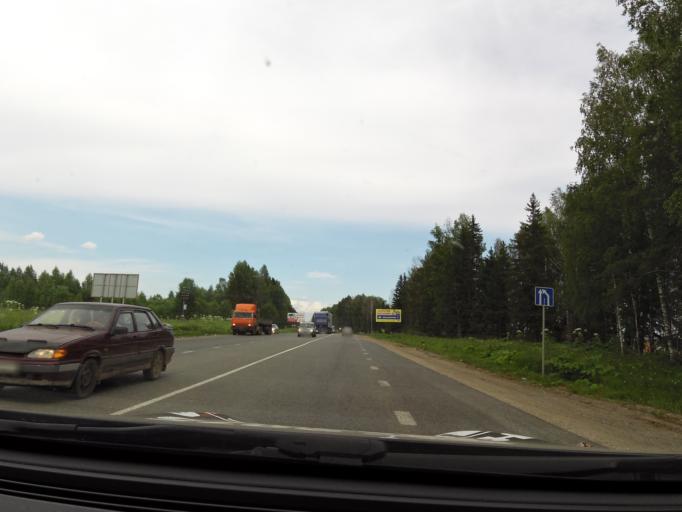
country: RU
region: Kirov
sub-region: Kirovo-Chepetskiy Rayon
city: Kirov
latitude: 58.6339
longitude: 49.8280
